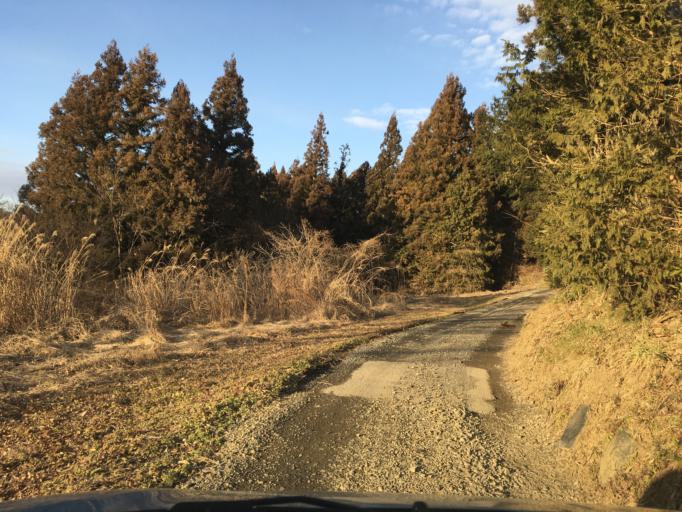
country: JP
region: Iwate
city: Ichinoseki
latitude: 38.8532
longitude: 141.2903
